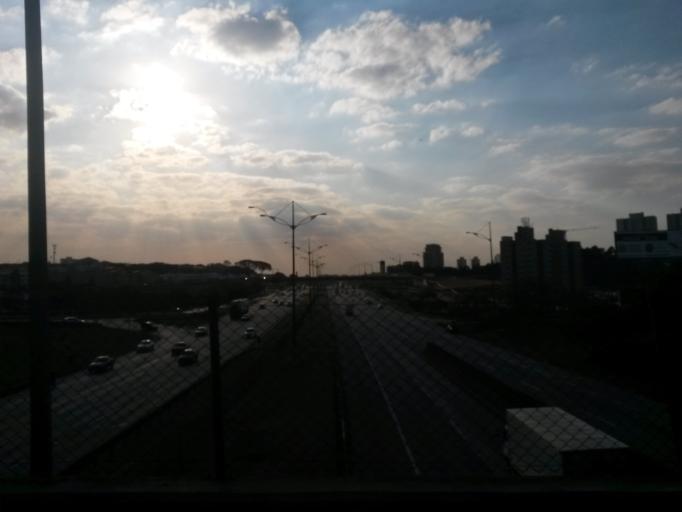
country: BR
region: Sao Paulo
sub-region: Sao Bernardo Do Campo
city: Sao Bernardo do Campo
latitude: -23.7244
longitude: -46.5519
